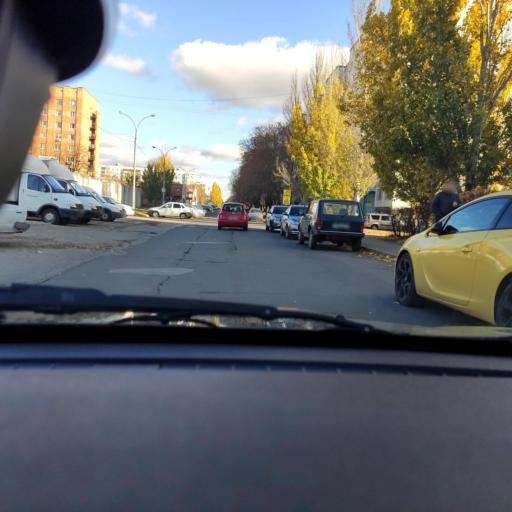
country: RU
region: Samara
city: Tol'yatti
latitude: 53.5328
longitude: 49.3233
